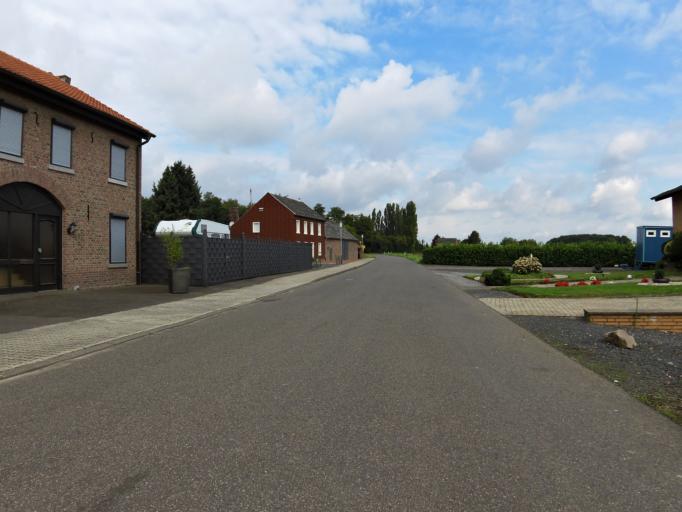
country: DE
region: North Rhine-Westphalia
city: Geilenkirchen
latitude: 50.9677
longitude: 6.0713
